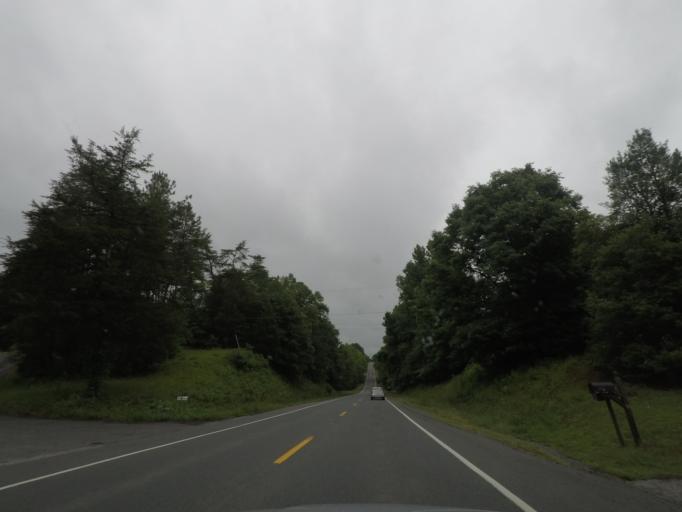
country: US
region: Virginia
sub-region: Fluvanna County
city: Palmyra
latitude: 37.8393
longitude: -78.2731
